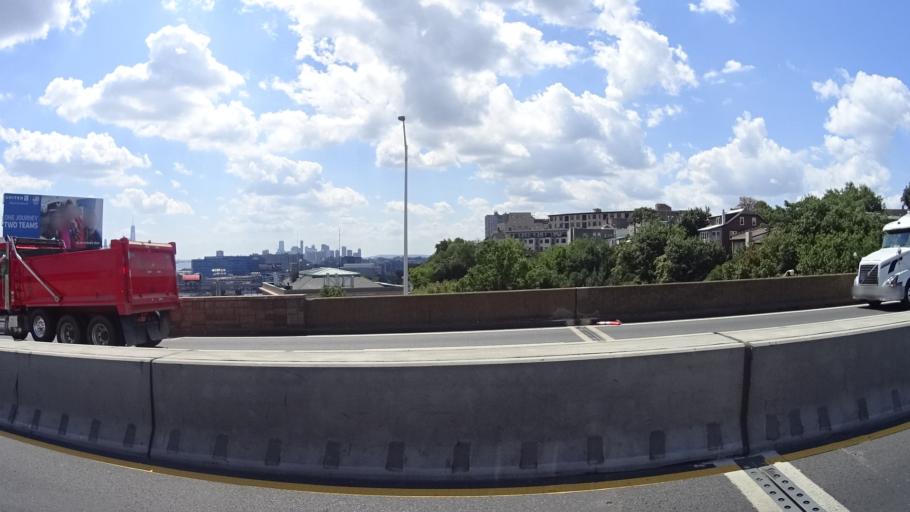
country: US
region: New Jersey
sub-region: Hudson County
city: Weehawken
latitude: 40.7684
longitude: -74.0226
